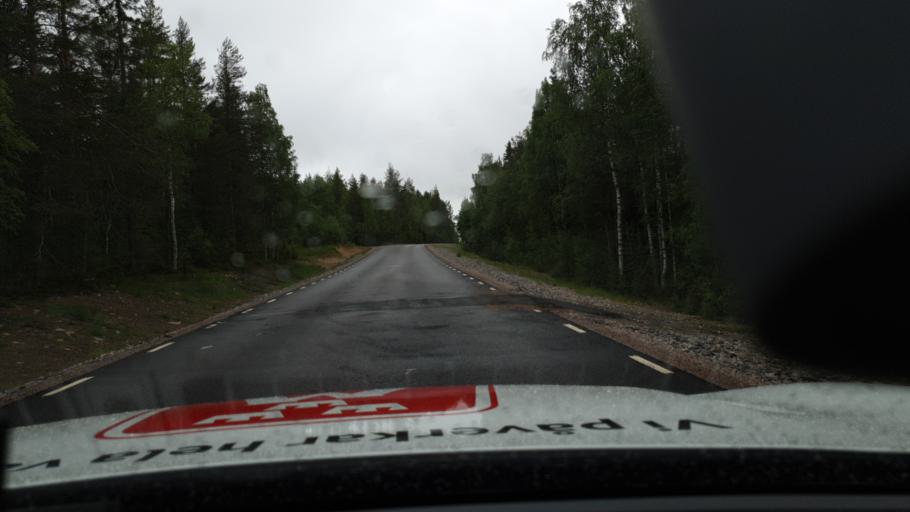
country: SE
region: Norrbotten
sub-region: Overtornea Kommun
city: OEvertornea
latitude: 66.4611
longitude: 23.4708
